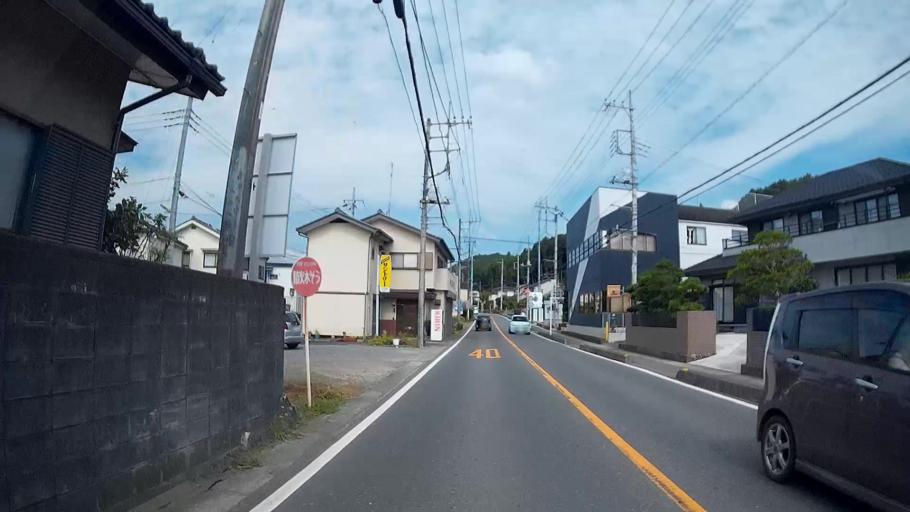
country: JP
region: Saitama
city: Hanno
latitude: 35.8590
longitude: 139.2995
